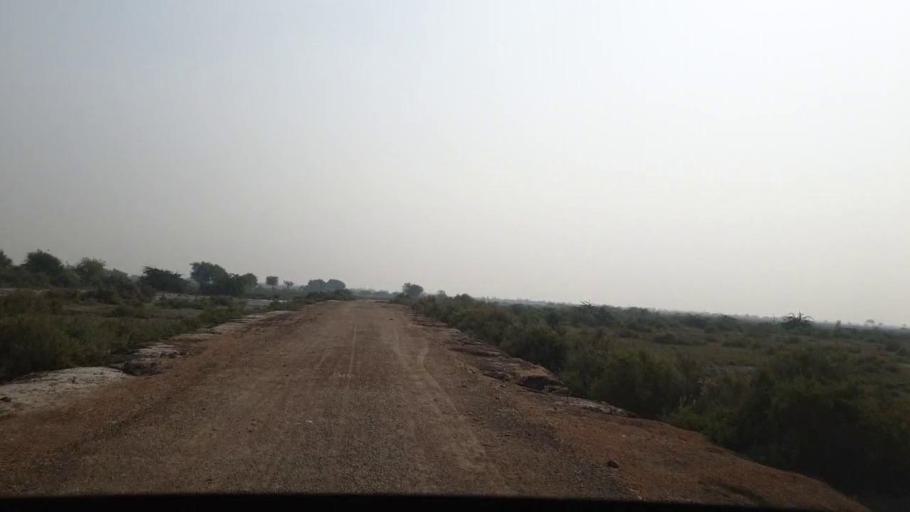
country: PK
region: Sindh
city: Jati
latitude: 24.2685
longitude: 68.4234
